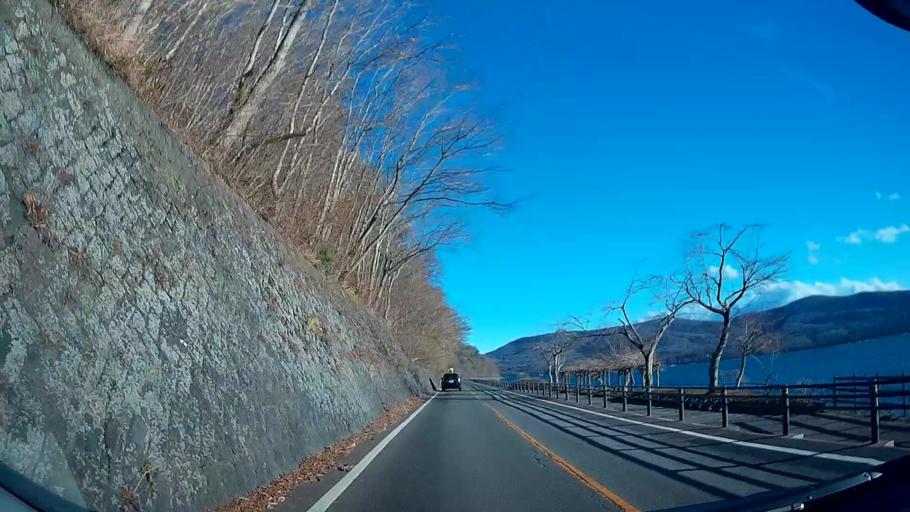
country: JP
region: Shizuoka
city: Gotemba
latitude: 35.4260
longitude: 138.8758
